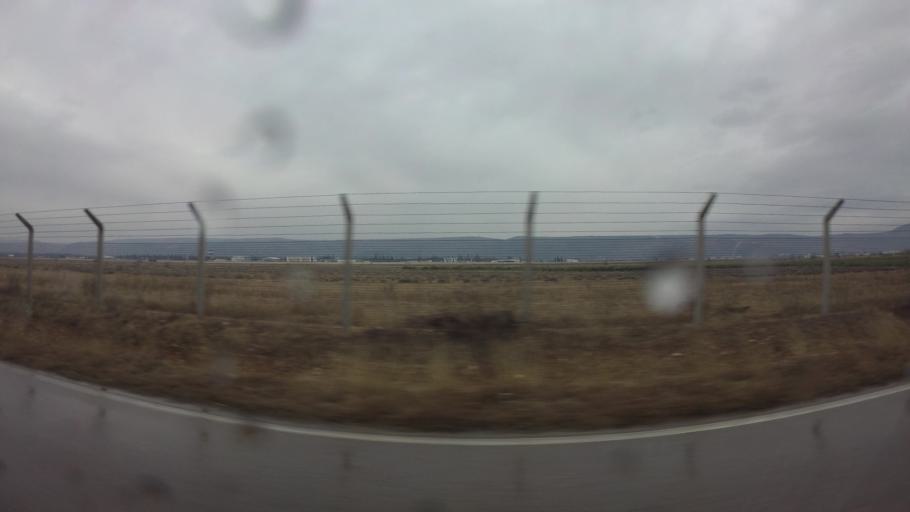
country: BA
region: Federation of Bosnia and Herzegovina
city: Rodoc
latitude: 43.2930
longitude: 17.8454
